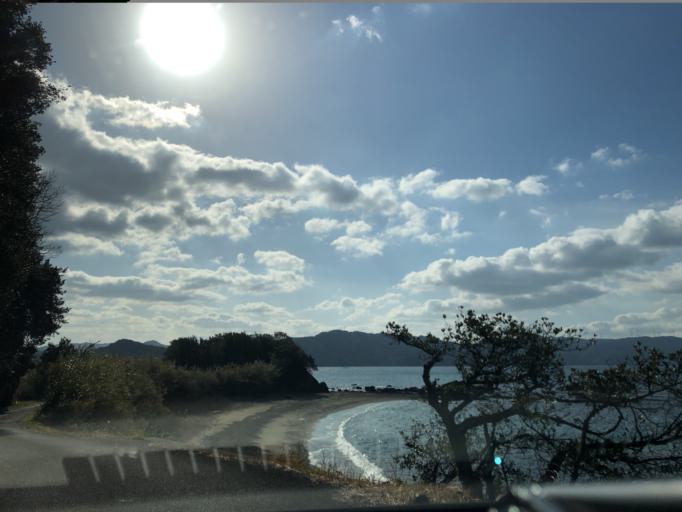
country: JP
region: Kochi
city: Sukumo
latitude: 32.9116
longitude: 132.6948
